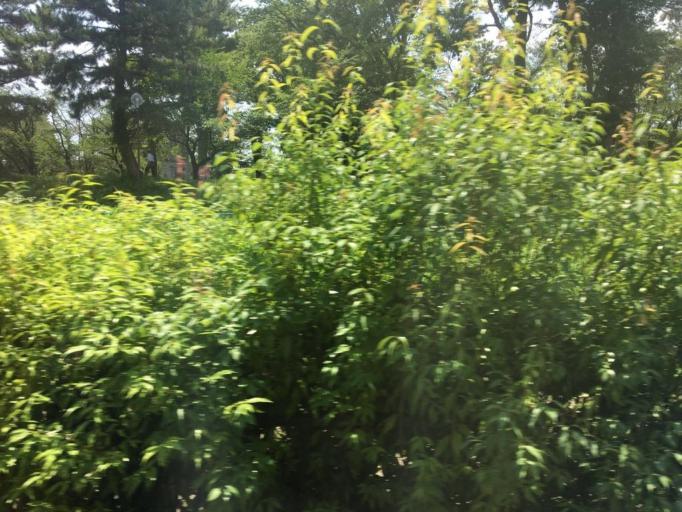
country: JP
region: Saitama
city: Menuma
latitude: 36.2626
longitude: 139.4137
